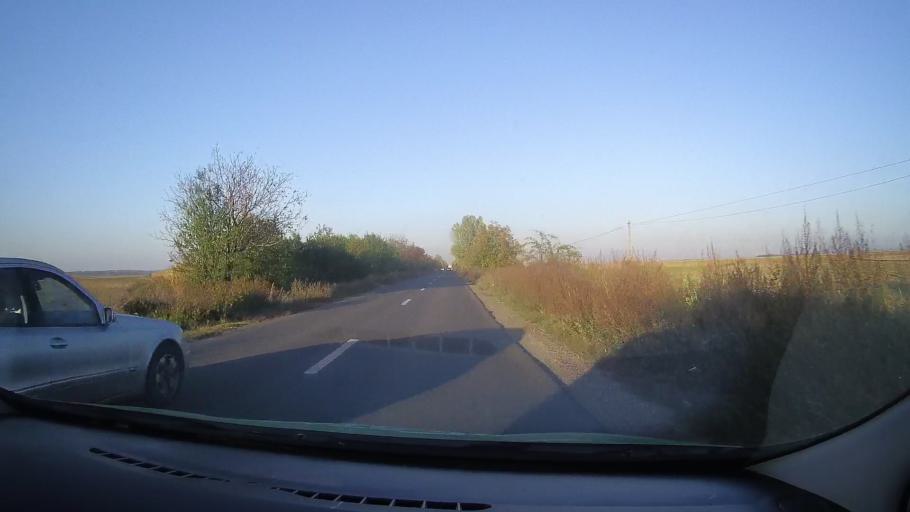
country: RO
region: Bihor
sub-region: Comuna Salard
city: Salard
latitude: 47.1925
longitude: 21.9971
